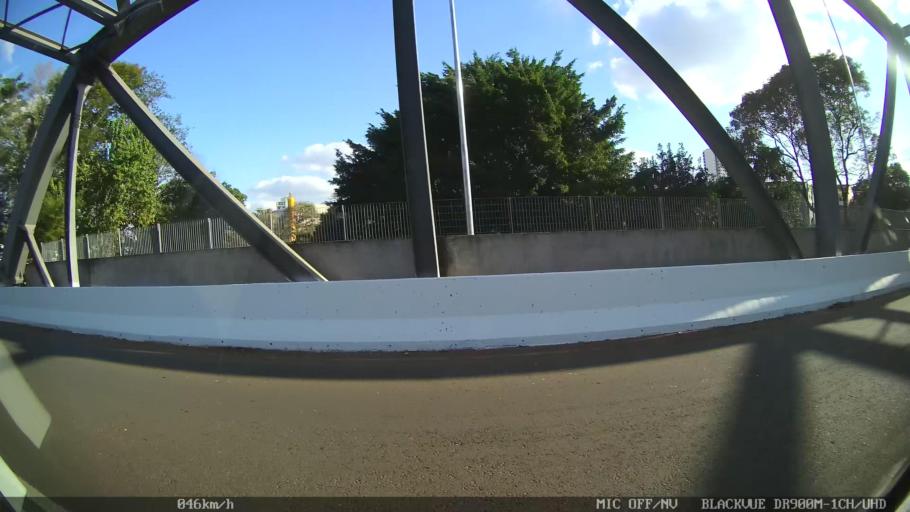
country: BR
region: Sao Paulo
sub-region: Santa Barbara D'Oeste
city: Santa Barbara d'Oeste
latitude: -22.7519
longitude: -47.4080
